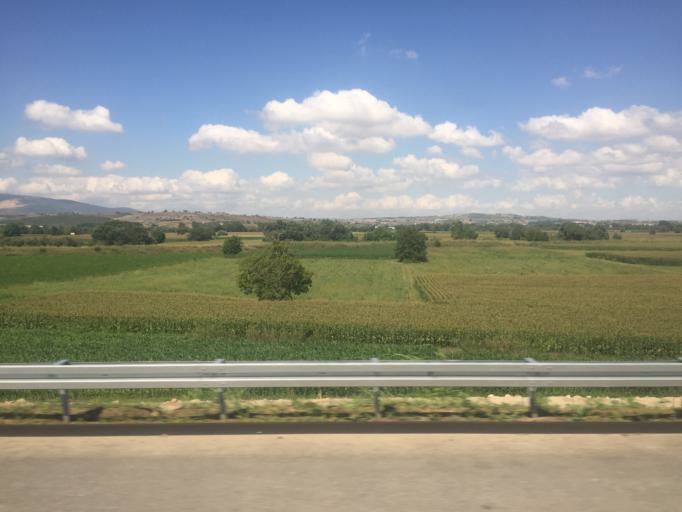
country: TR
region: Balikesir
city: Gobel
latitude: 40.0032
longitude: 28.1940
